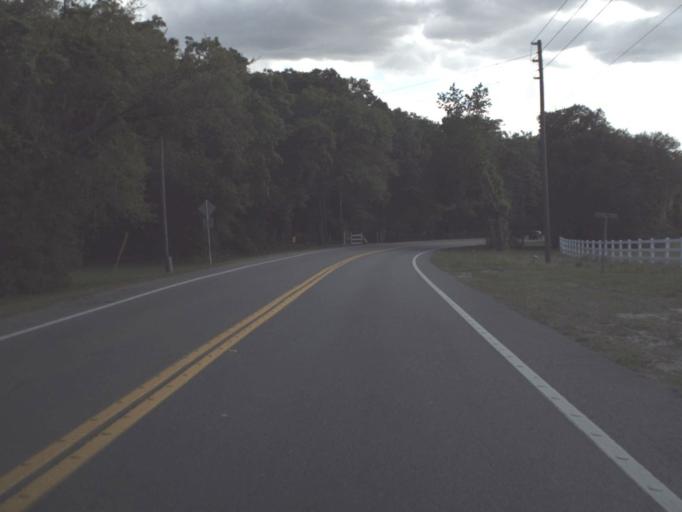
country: US
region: Florida
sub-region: Lake County
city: Mount Plymouth
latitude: 28.8068
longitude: -81.5695
